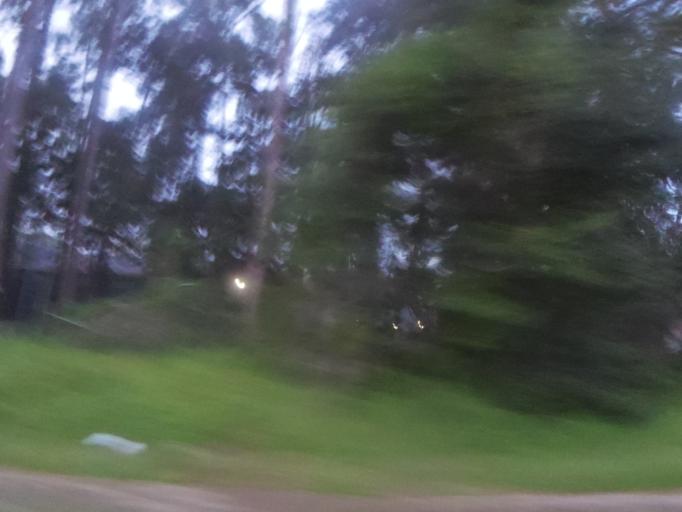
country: US
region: Florida
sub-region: Duval County
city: Jacksonville
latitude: 30.2437
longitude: -81.6133
